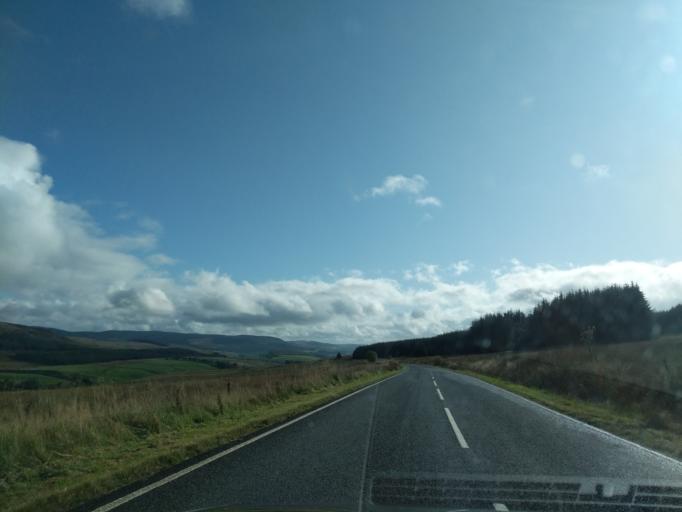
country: GB
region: Scotland
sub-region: Dumfries and Galloway
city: Moffat
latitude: 55.3838
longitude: -3.4848
